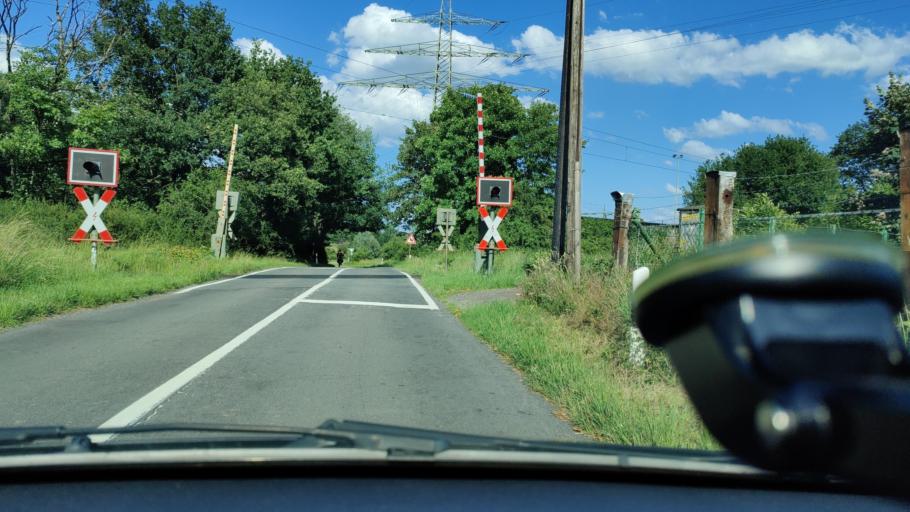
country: DE
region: North Rhine-Westphalia
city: Rheinberg
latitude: 51.5513
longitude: 6.5721
